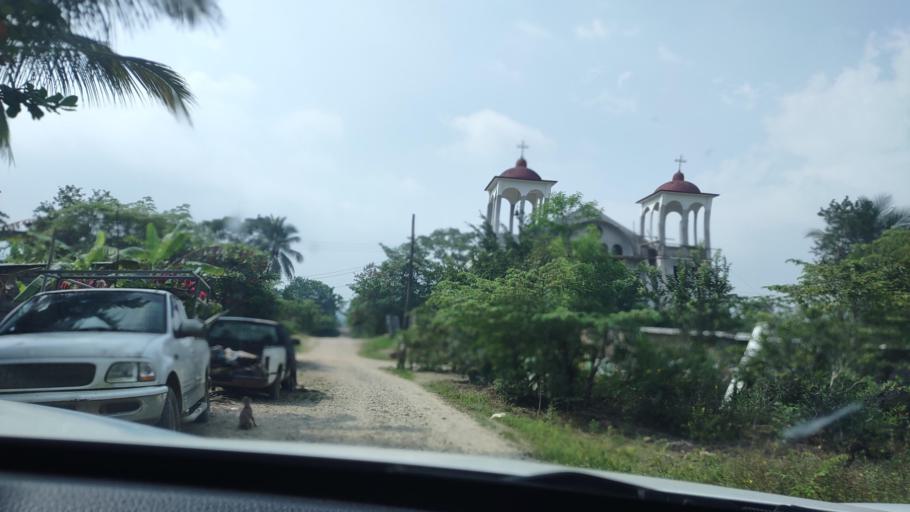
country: MX
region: Veracruz
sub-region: Uxpanapa
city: Poblado 10
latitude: 17.5461
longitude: -94.2893
